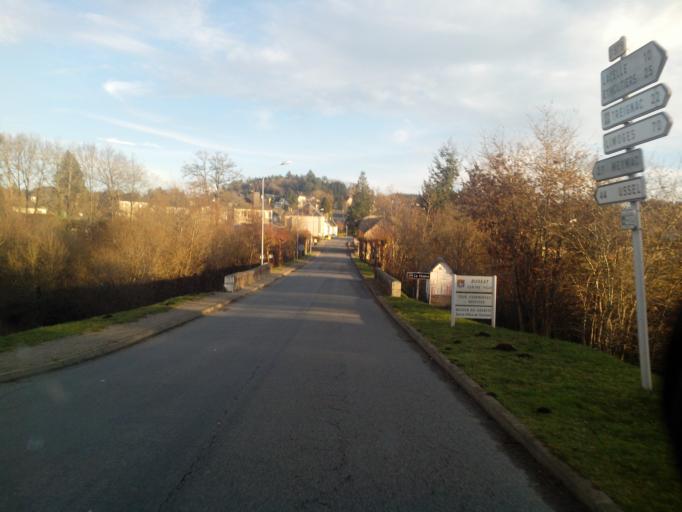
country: FR
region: Limousin
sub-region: Departement de la Correze
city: Bugeat
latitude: 45.6011
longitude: 1.9214
